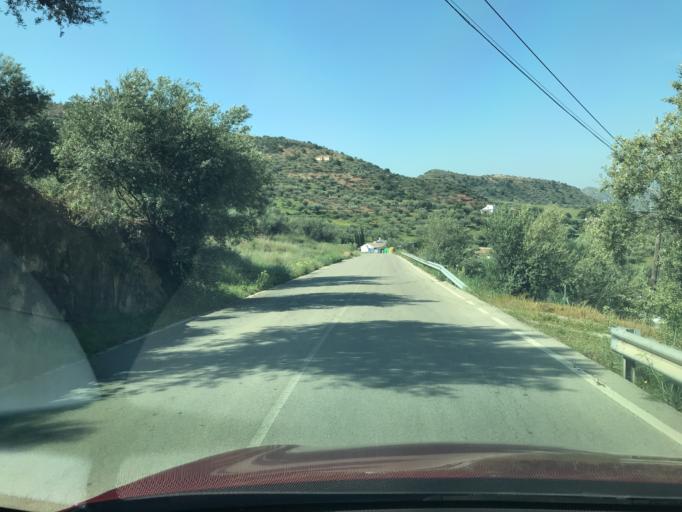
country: ES
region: Andalusia
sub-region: Provincia de Malaga
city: Alcaucin
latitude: 36.9006
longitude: -4.1193
